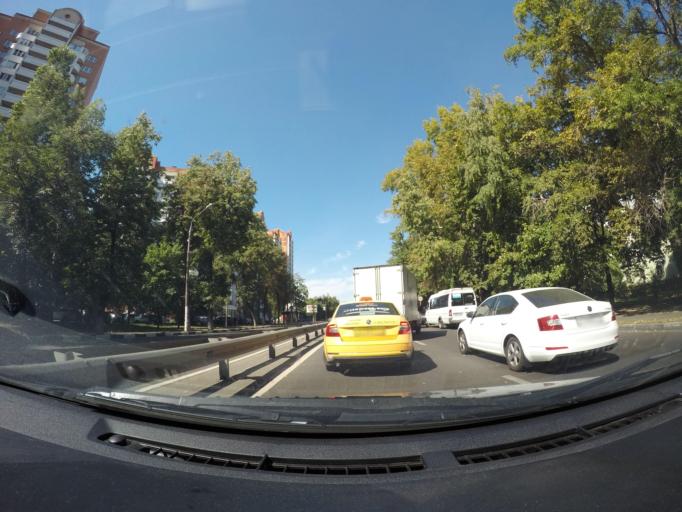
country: RU
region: Moscow
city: Zhulebino
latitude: 55.6917
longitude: 37.8674
